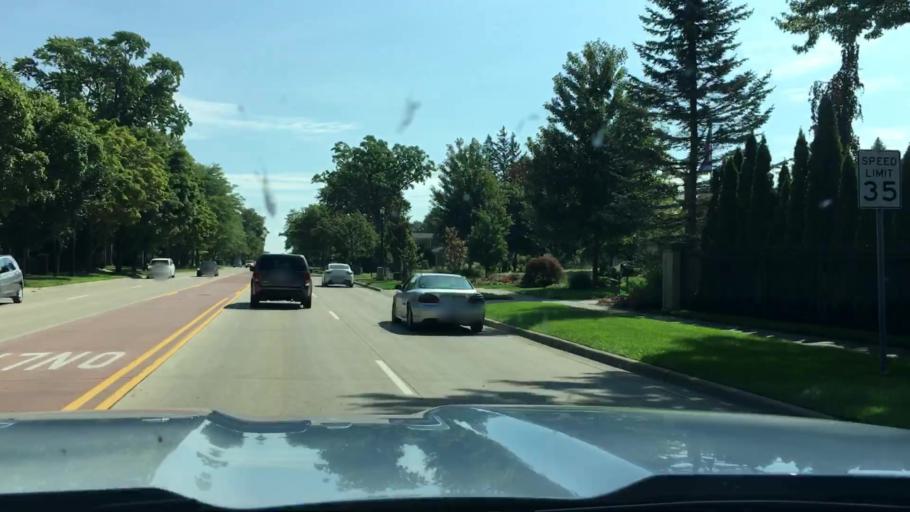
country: US
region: Michigan
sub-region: Bay County
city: Bay City
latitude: 43.5959
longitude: -83.8621
